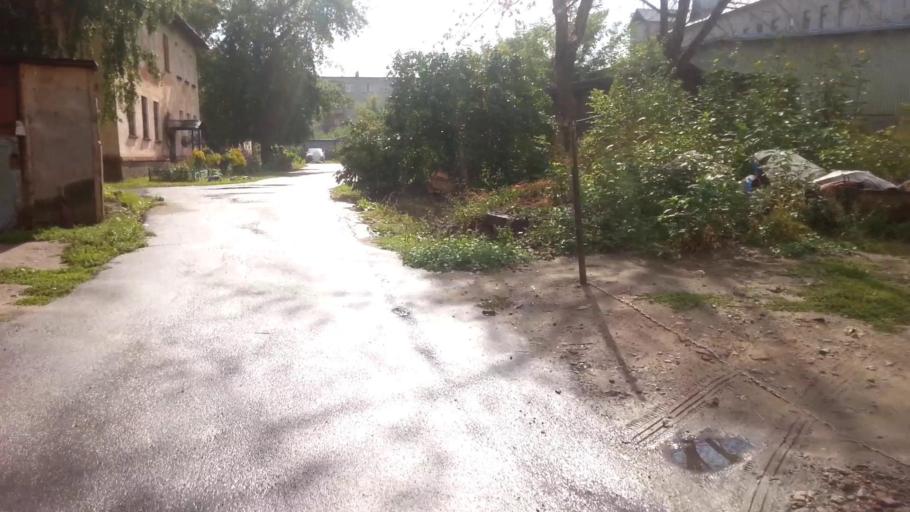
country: RU
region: Altai Krai
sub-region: Gorod Barnaulskiy
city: Barnaul
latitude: 53.3475
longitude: 83.7577
